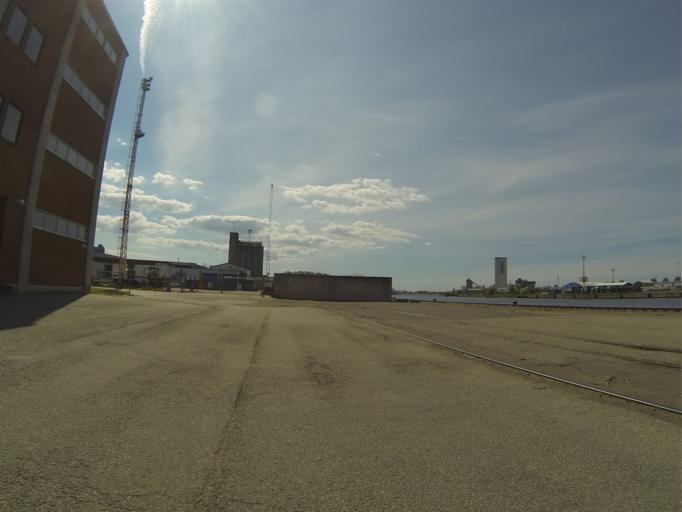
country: SE
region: Skane
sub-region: Malmo
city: Malmoe
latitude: 55.6230
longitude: 13.0315
